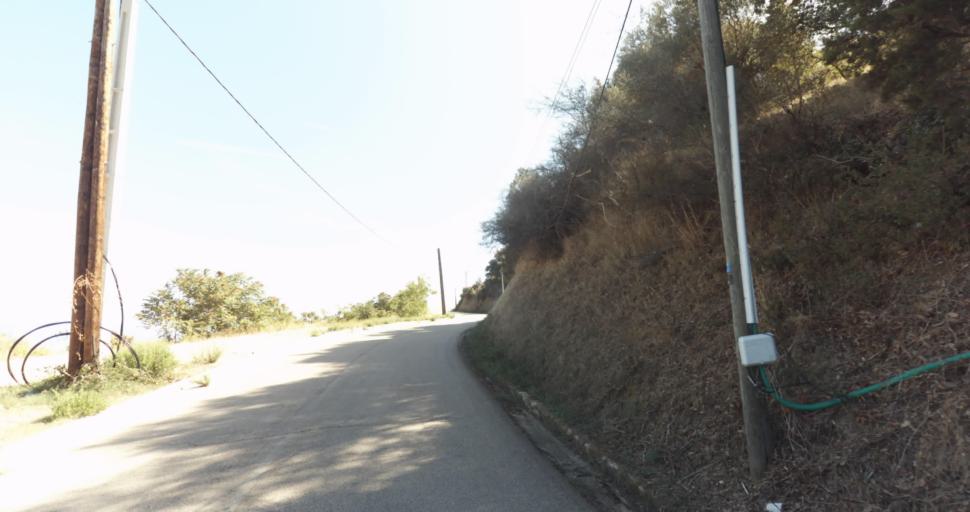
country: FR
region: Corsica
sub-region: Departement de la Corse-du-Sud
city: Ajaccio
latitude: 41.9254
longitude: 8.7126
